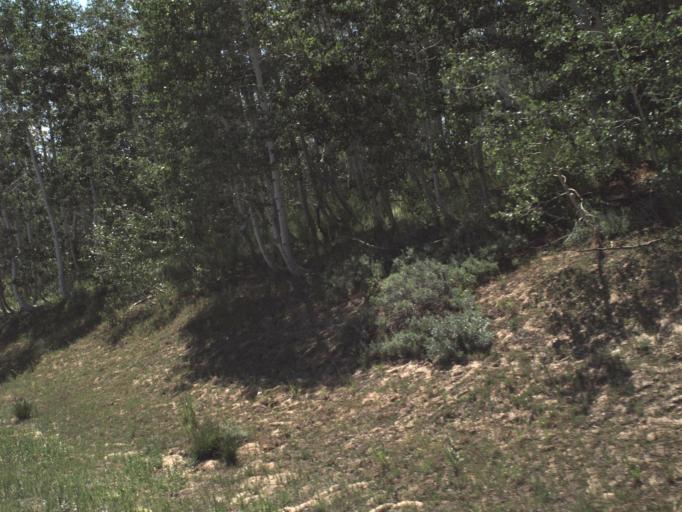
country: US
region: Utah
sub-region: Weber County
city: Wolf Creek
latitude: 41.4515
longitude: -111.5023
